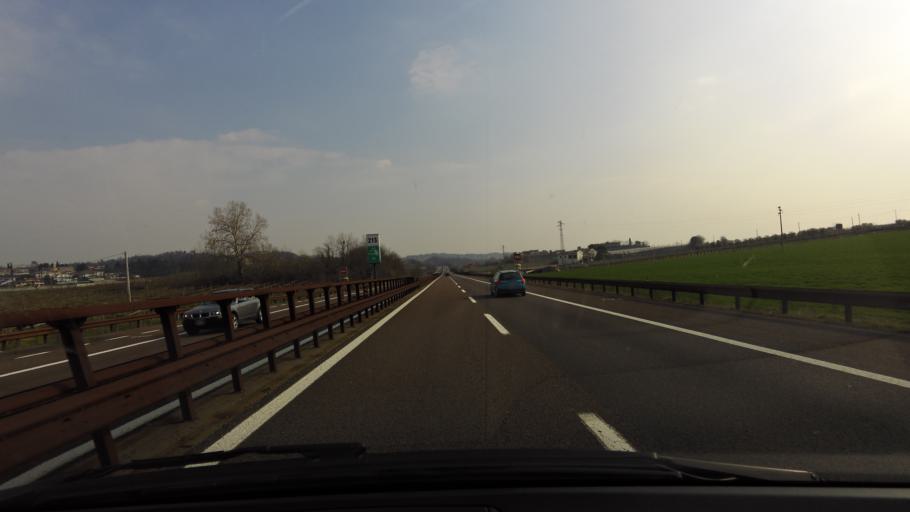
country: IT
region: Veneto
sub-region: Provincia di Verona
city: Pastrengo
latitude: 45.4959
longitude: 10.7876
